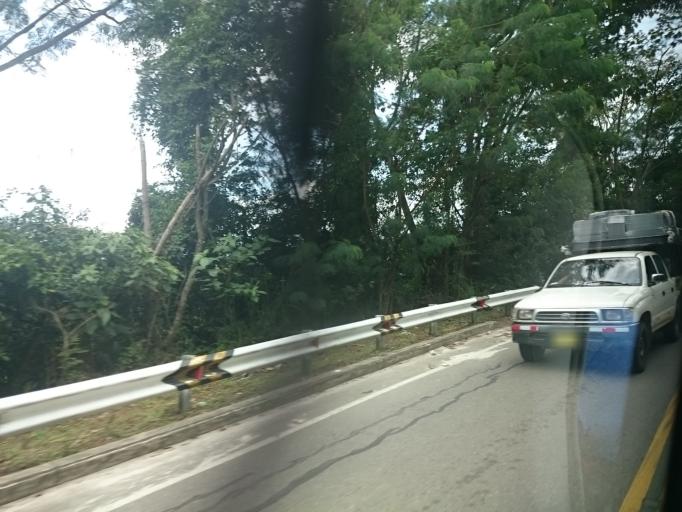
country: PE
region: San Martin
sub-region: Provincia de San Martin
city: Tarapoto
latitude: -6.4655
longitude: -76.3187
